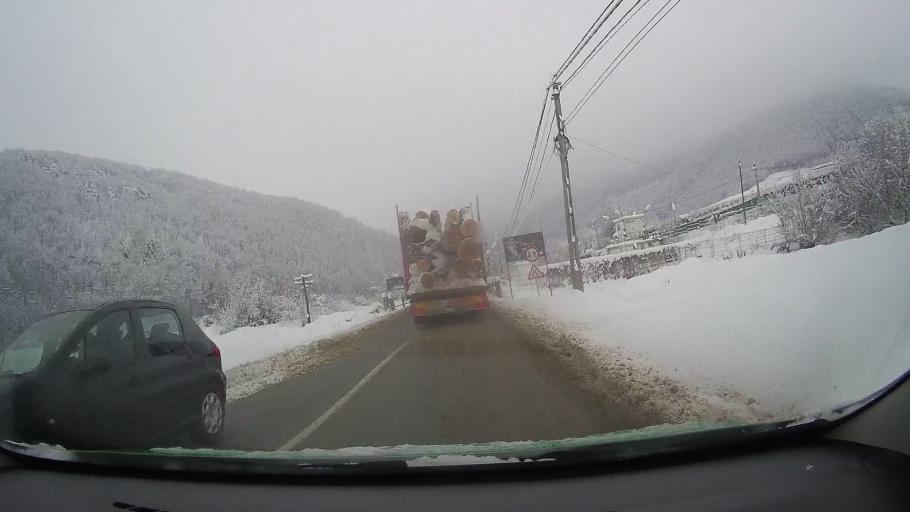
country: RO
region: Sibiu
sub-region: Comuna Orlat
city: Orlat
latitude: 45.7652
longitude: 23.9401
